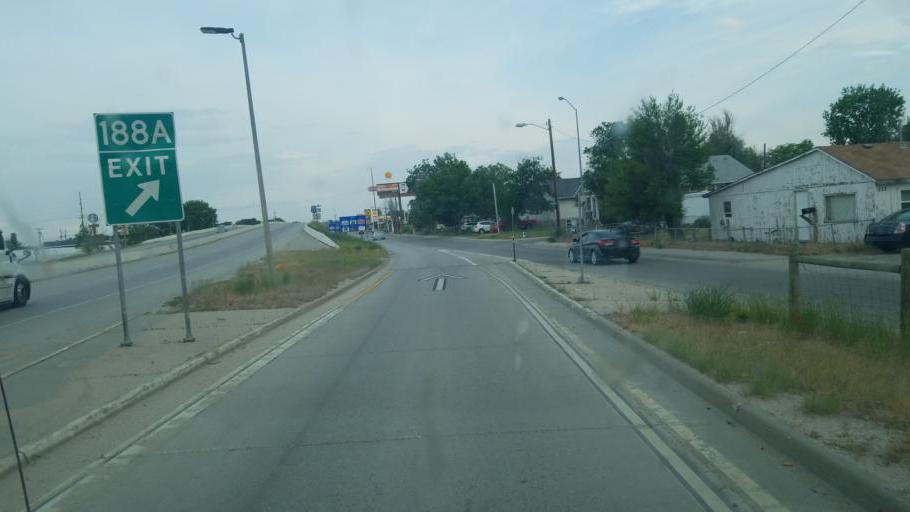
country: US
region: Wyoming
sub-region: Natrona County
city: Casper
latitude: 42.8572
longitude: -106.3214
